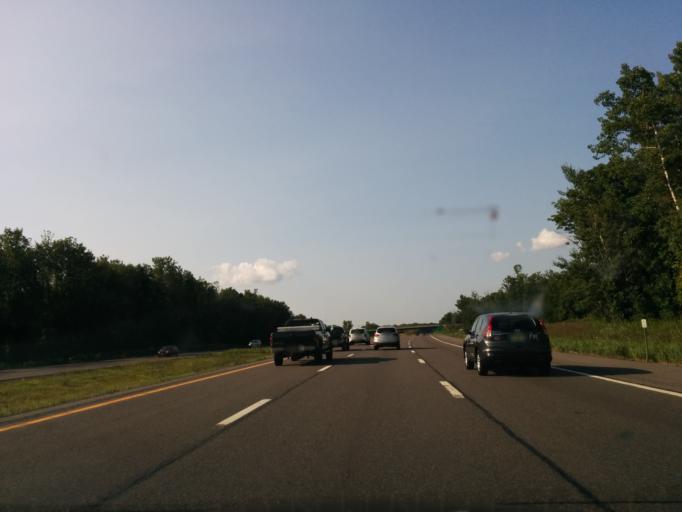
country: US
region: New York
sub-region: Onondaga County
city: Brewerton
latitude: 43.2123
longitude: -76.1292
